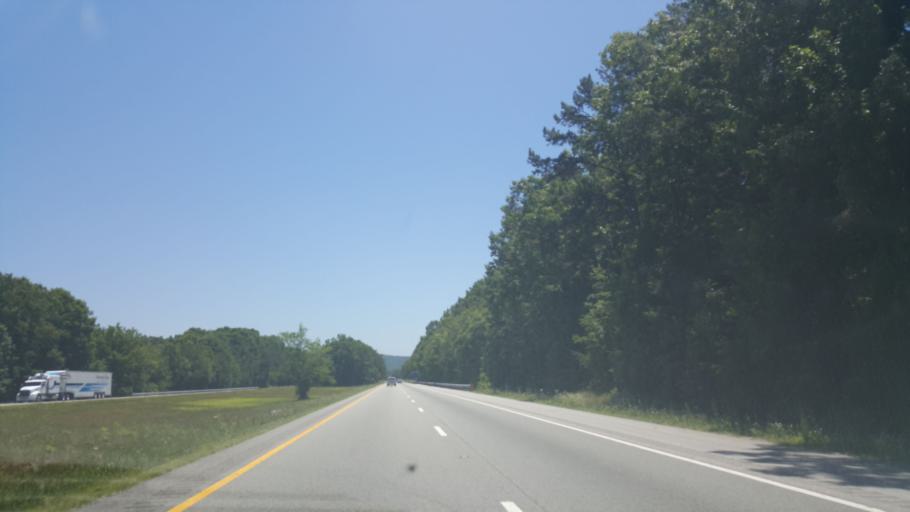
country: US
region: Tennessee
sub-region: Roane County
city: Rockwood
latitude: 35.8973
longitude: -84.7642
